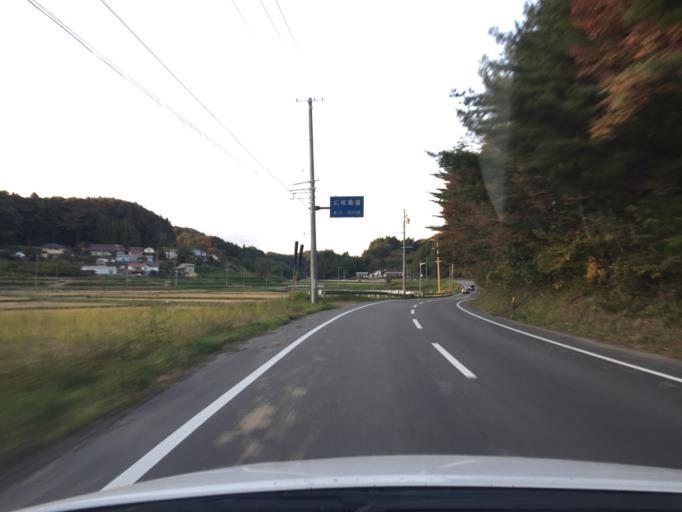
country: JP
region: Fukushima
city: Sukagawa
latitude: 37.3394
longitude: 140.4418
